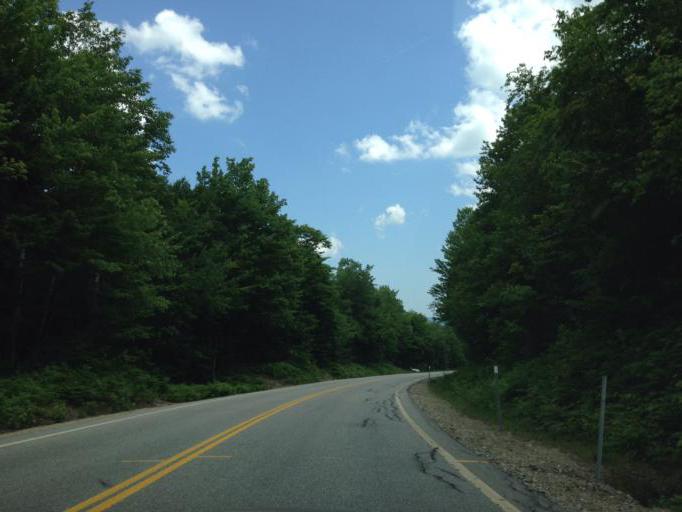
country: US
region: New Hampshire
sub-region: Carroll County
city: Sandwich
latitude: 44.0223
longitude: -71.4409
